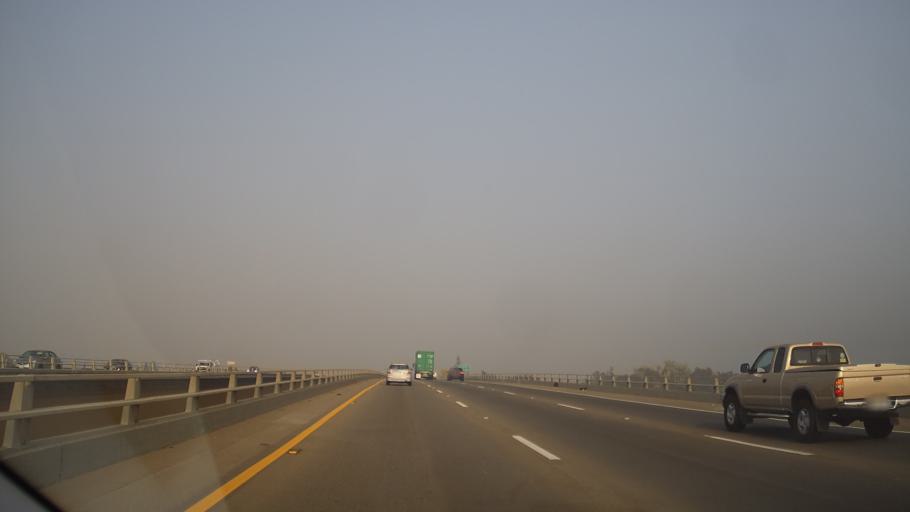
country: US
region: California
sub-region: Yolo County
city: West Sacramento
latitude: 38.5968
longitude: -121.5484
